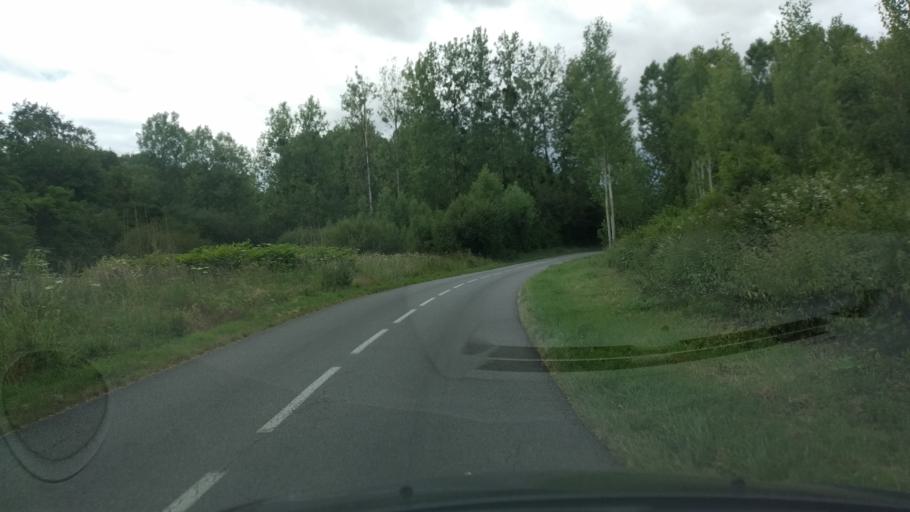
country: FR
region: Poitou-Charentes
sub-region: Departement de la Vienne
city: Vouille
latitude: 46.6309
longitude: 0.1696
